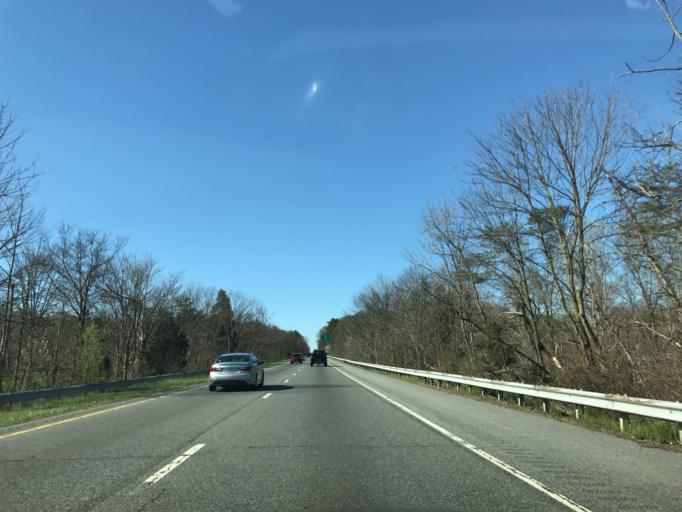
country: US
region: Maryland
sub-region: Howard County
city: Hanover
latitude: 39.1824
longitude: -76.7204
